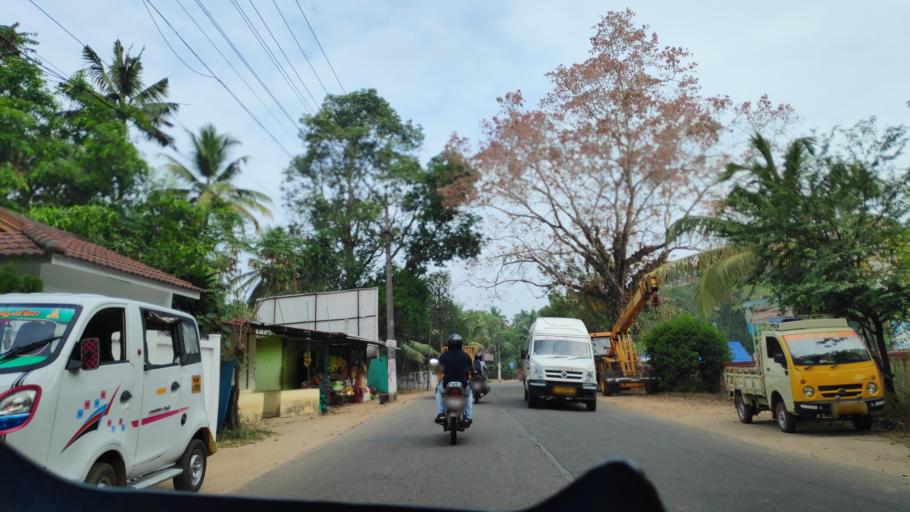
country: IN
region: Kerala
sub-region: Alappuzha
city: Vayalar
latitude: 9.7143
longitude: 76.3590
